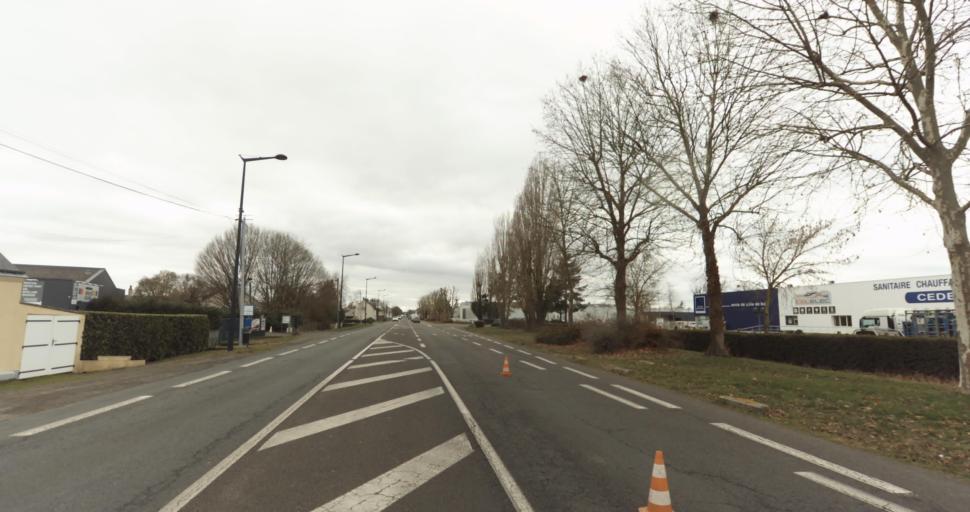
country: FR
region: Pays de la Loire
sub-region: Departement de Maine-et-Loire
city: Saumur
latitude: 47.2793
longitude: -0.0560
